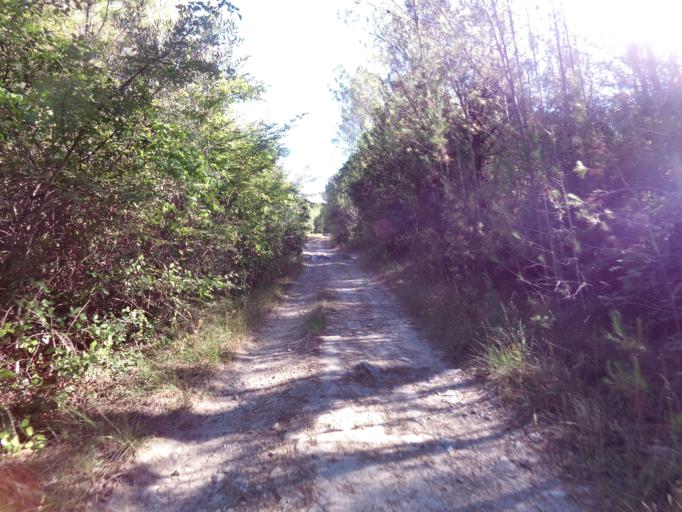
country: FR
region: Languedoc-Roussillon
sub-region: Departement du Gard
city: Aigues-Vives
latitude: 43.7570
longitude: 4.1883
